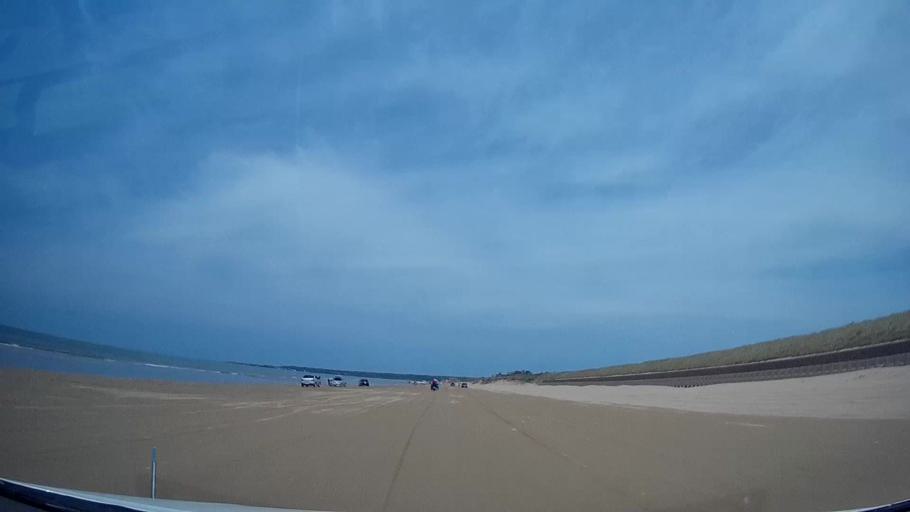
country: JP
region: Ishikawa
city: Hakui
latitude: 36.8800
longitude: 136.7622
